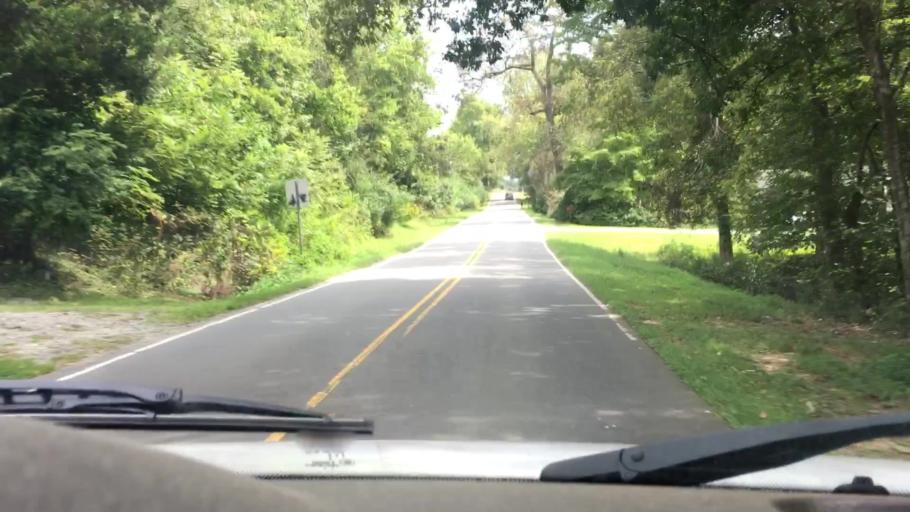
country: US
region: North Carolina
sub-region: Gaston County
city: Davidson
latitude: 35.4996
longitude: -80.8280
